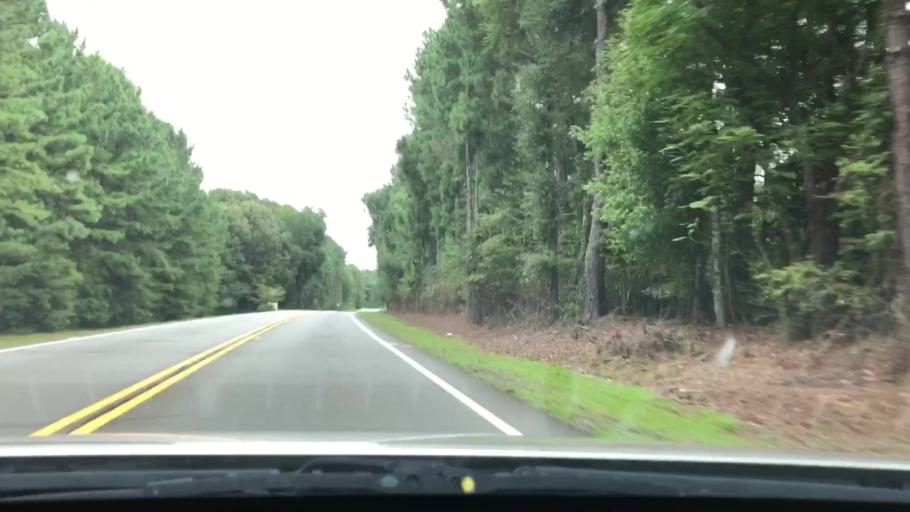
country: US
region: Georgia
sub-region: Upson County
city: Hannahs Mill
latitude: 33.0210
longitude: -84.4975
